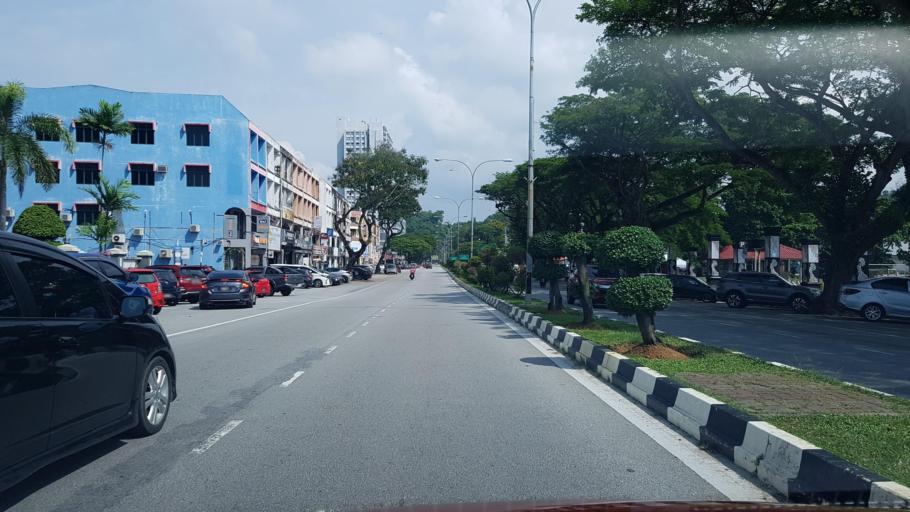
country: MY
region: Terengganu
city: Kuala Terengganu
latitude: 5.3263
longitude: 103.1412
